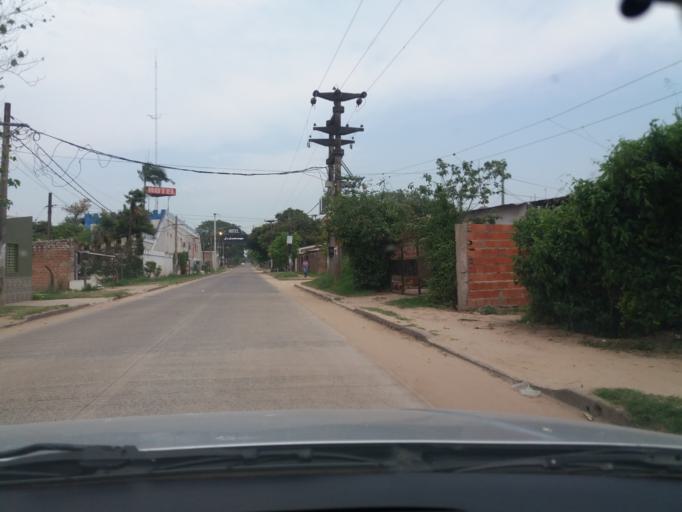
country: AR
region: Corrientes
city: Corrientes
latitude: -27.5126
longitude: -58.8035
